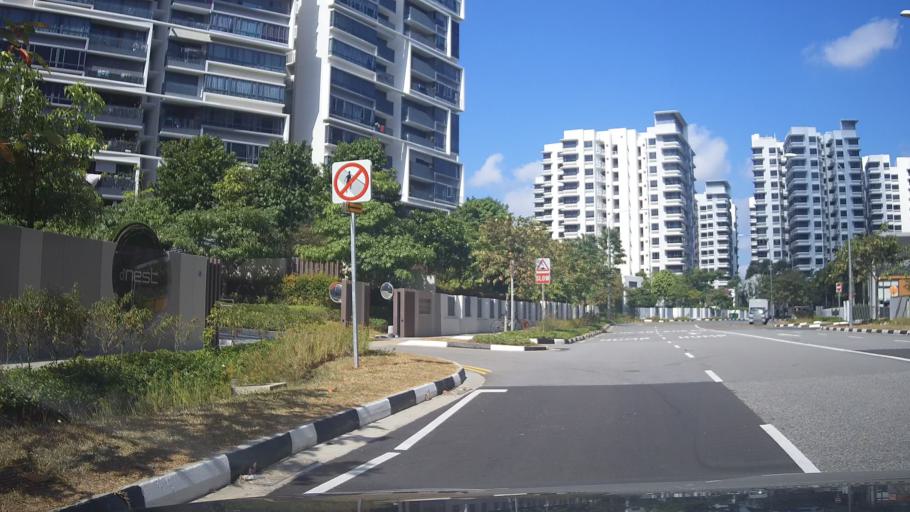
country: MY
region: Johor
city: Kampung Pasir Gudang Baru
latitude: 1.3706
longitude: 103.9465
